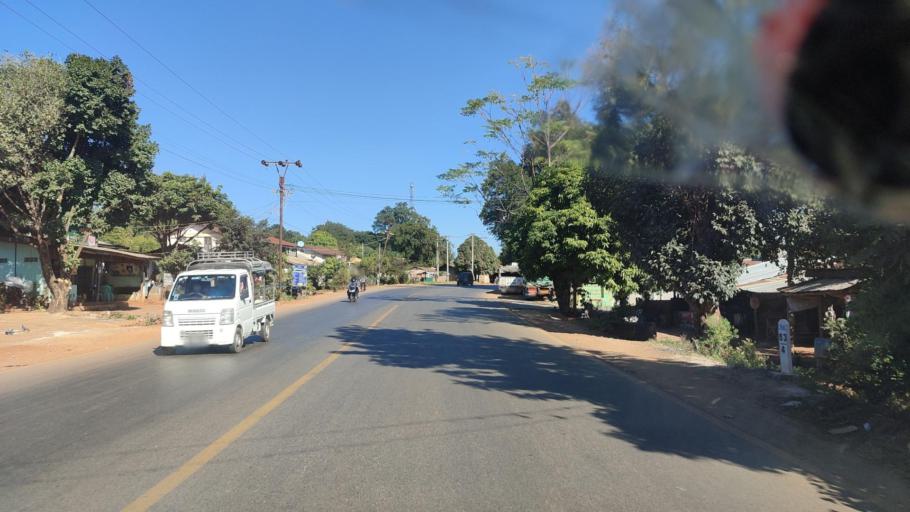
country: MM
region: Mandalay
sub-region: Pyin Oo Lwin District
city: Pyin Oo Lwin
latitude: 22.0946
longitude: 96.5913
